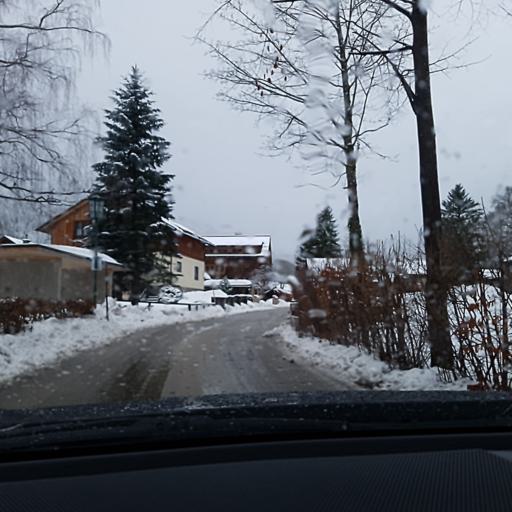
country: AT
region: Styria
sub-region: Politischer Bezirk Liezen
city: Altaussee
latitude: 47.6369
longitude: 13.7675
